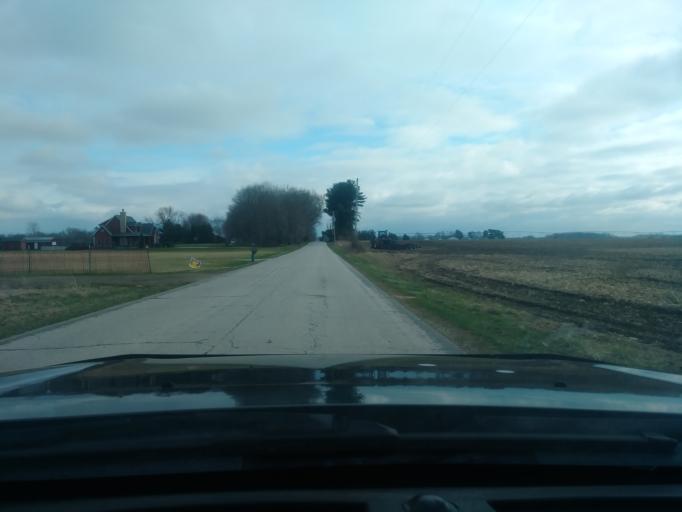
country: US
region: Indiana
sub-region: LaPorte County
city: LaPorte
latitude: 41.5758
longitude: -86.7982
